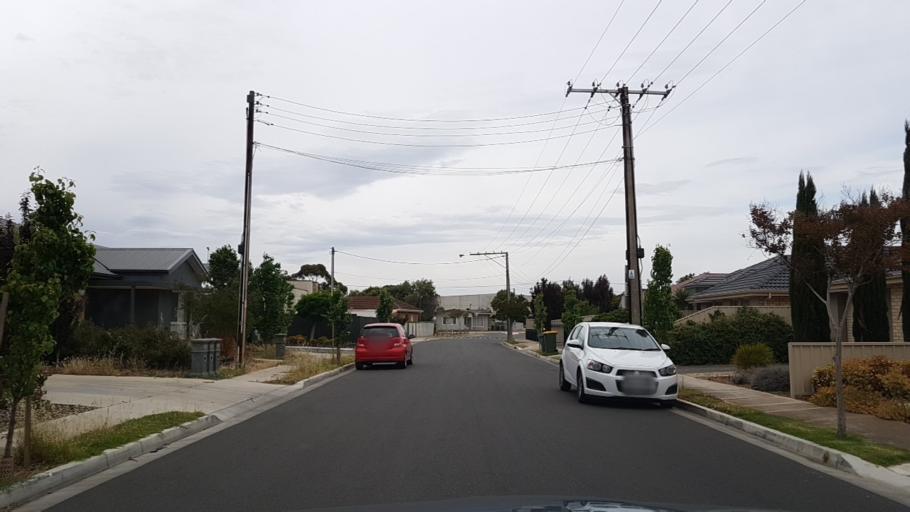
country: AU
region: South Australia
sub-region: Charles Sturt
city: Findon
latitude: -34.8991
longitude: 138.5403
